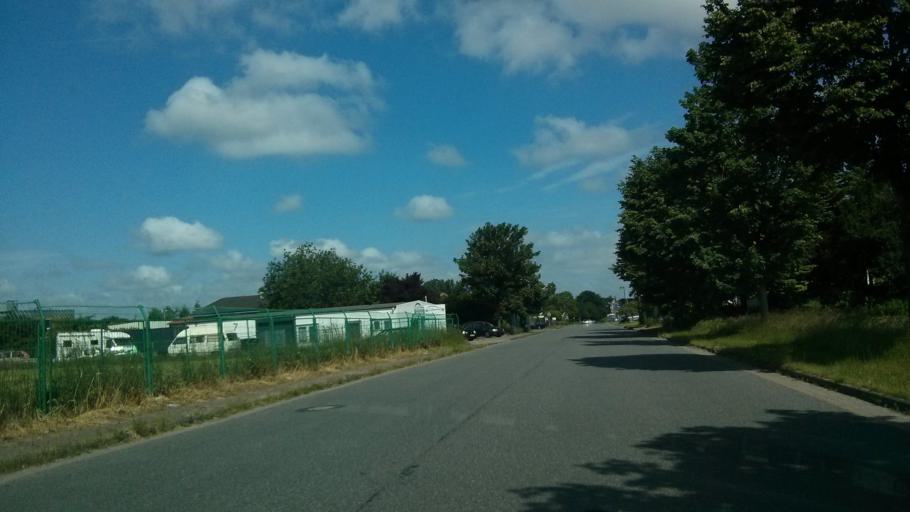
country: DE
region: Lower Saxony
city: Loxstedt
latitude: 53.4771
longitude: 8.6557
